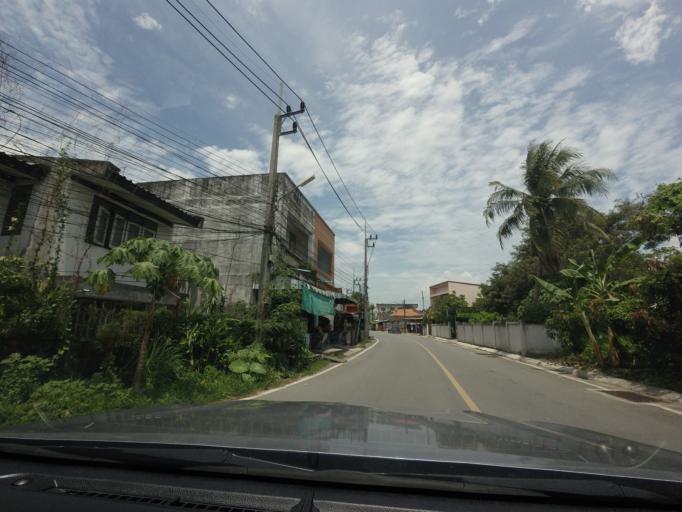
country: TH
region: Yala
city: Yala
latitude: 6.5462
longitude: 101.2944
